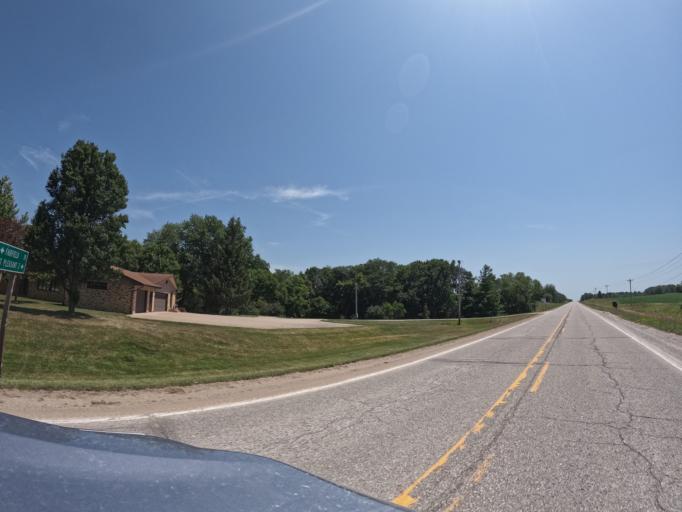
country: US
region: Iowa
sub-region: Henry County
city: Mount Pleasant
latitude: 40.9662
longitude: -91.6124
